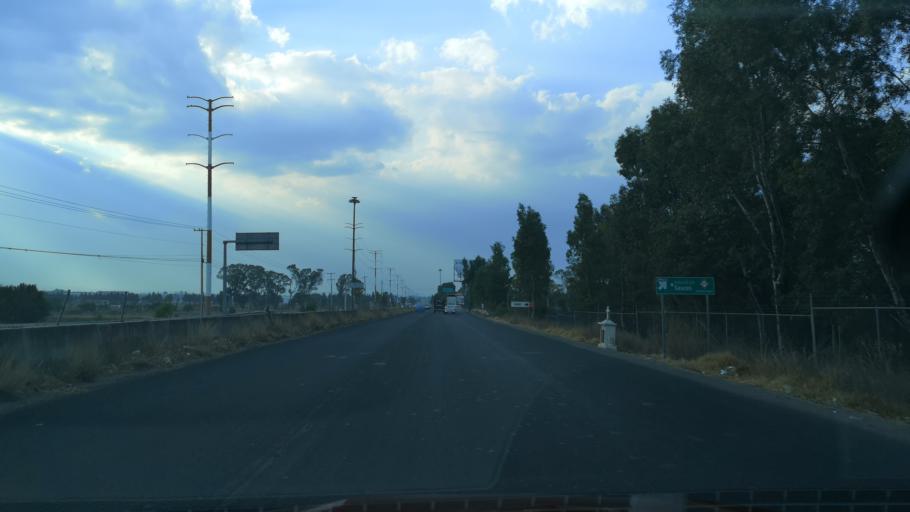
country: MX
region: Puebla
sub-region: Juan C. Bonilla
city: Santa Maria Zacatepec
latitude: 19.1301
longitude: -98.3715
